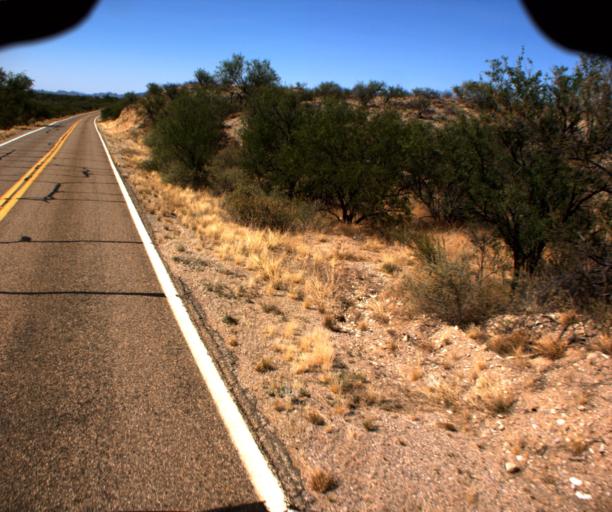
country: US
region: Arizona
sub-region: Pima County
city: Three Points
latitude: 31.9139
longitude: -111.3903
